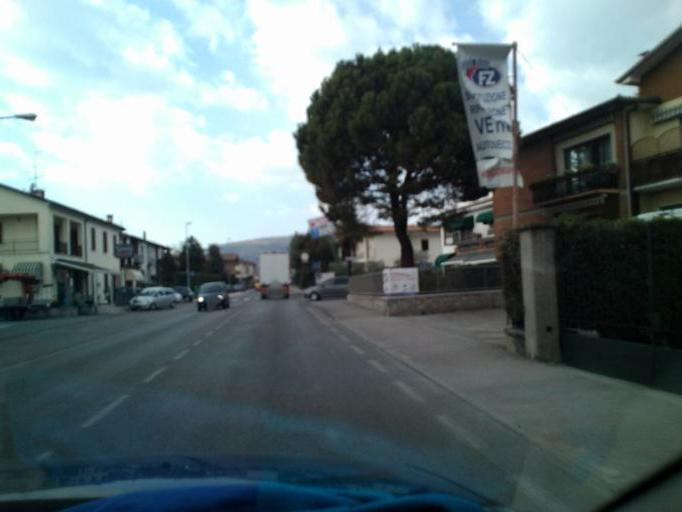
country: IT
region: Veneto
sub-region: Provincia di Verona
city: San Pietro in Cariano
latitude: 45.5184
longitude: 10.8903
